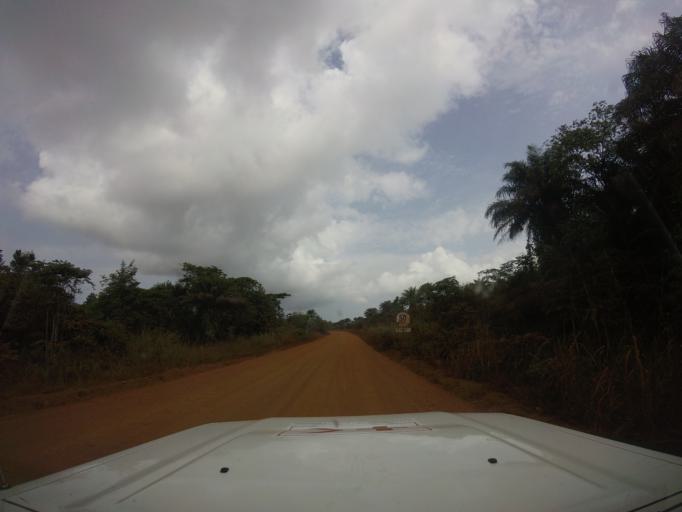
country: LR
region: Grand Cape Mount
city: Robertsport
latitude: 6.7057
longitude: -11.2940
